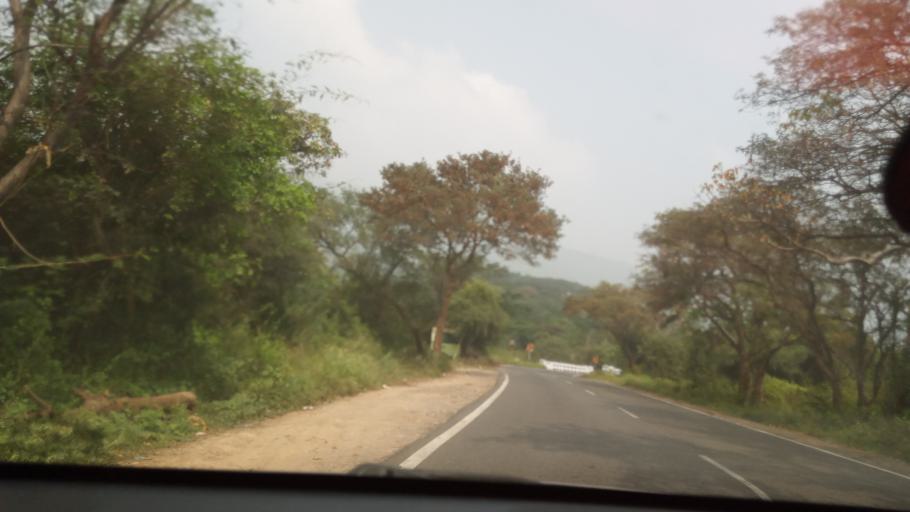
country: IN
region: Tamil Nadu
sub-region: Erode
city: Sathyamangalam
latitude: 11.5813
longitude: 77.1326
